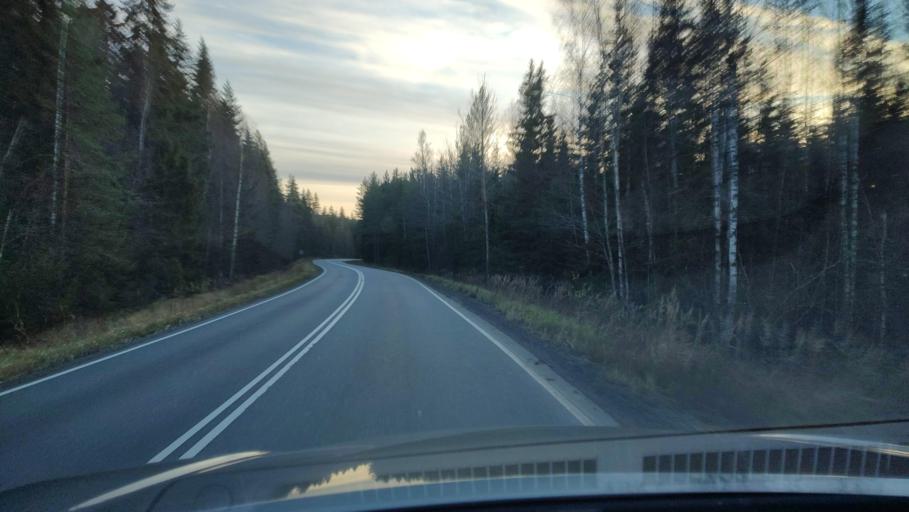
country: FI
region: Southern Ostrobothnia
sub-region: Suupohja
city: Karijoki
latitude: 62.2746
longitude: 21.5667
